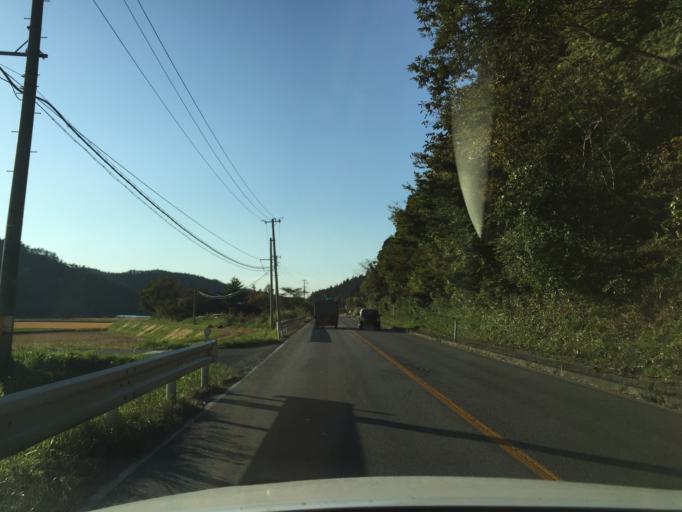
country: JP
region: Fukushima
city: Iwaki
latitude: 37.1092
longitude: 140.7659
